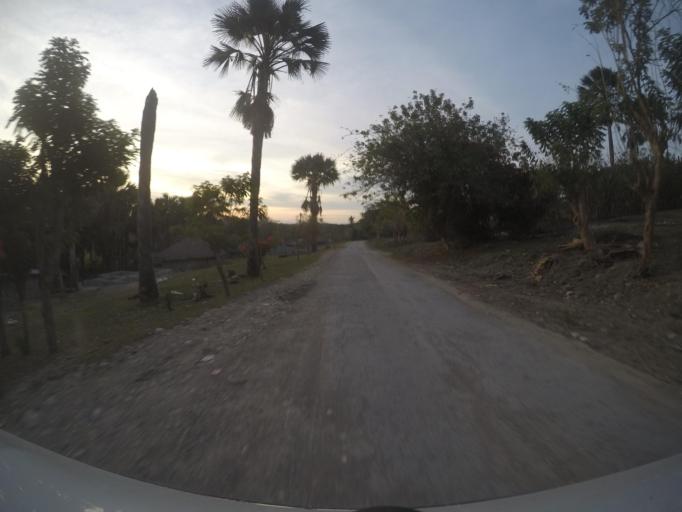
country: TL
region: Viqueque
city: Viqueque
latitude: -8.9232
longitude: 126.3982
